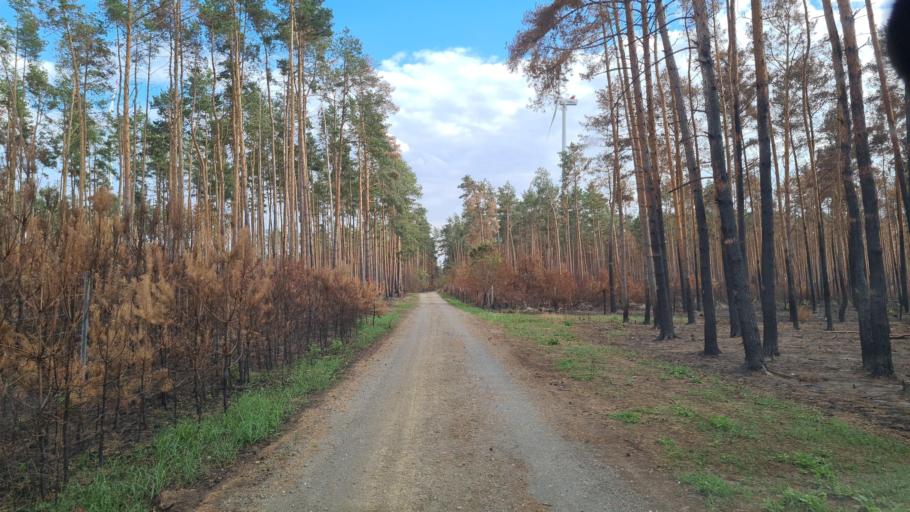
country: DE
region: Saxony
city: Arzberg
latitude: 51.5634
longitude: 13.1825
